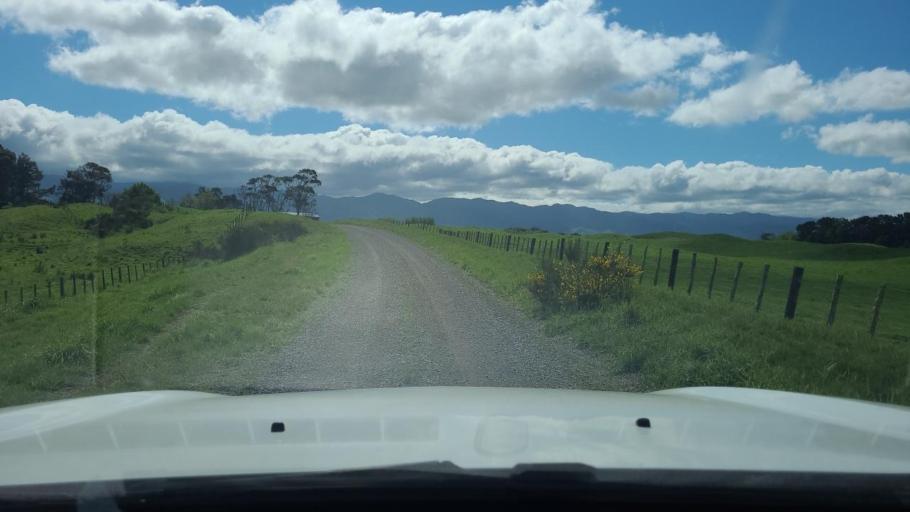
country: NZ
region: Wellington
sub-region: Upper Hutt City
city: Upper Hutt
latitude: -41.2361
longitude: 175.2948
